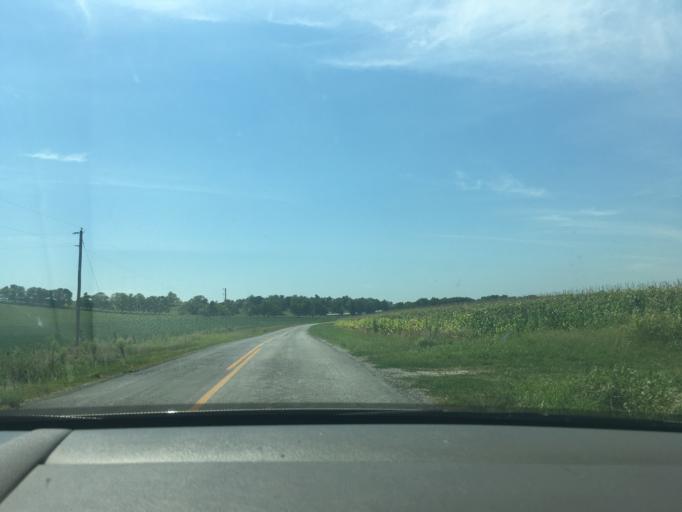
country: US
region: Missouri
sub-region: Gentry County
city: Stanberry
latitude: 40.2328
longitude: -94.7131
